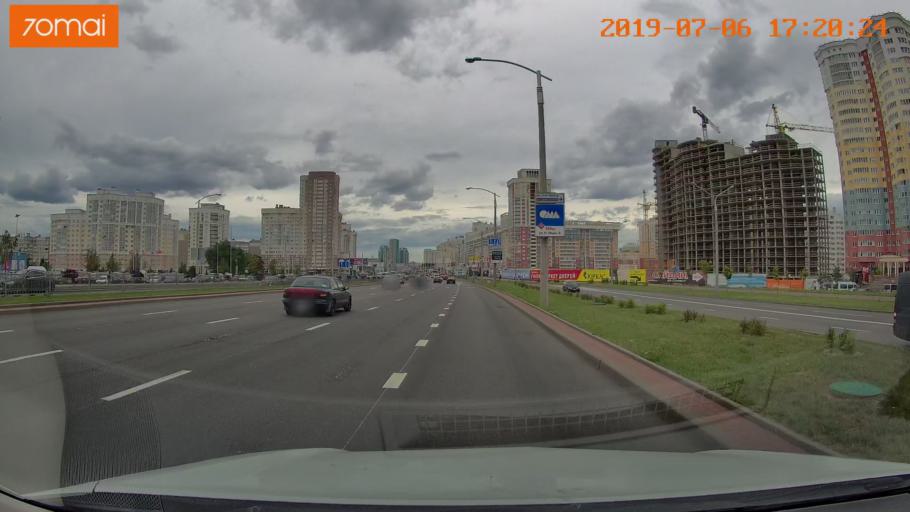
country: BY
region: Minsk
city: Shchomyslitsa
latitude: 53.8434
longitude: 27.4760
